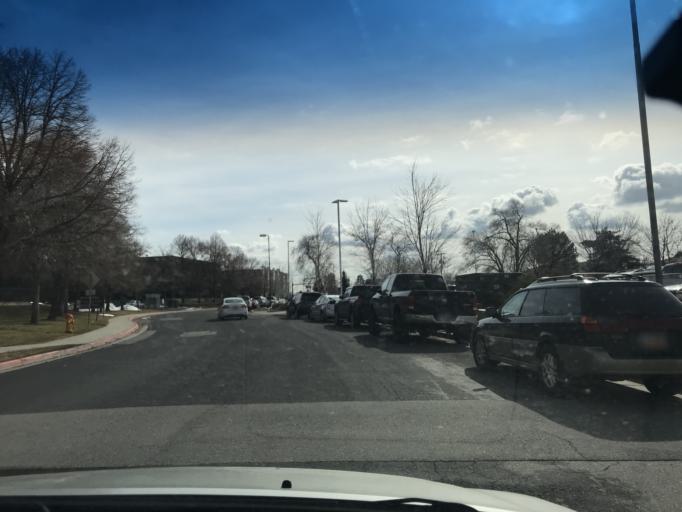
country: US
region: Utah
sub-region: Salt Lake County
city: Salt Lake City
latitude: 40.7737
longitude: -111.9475
